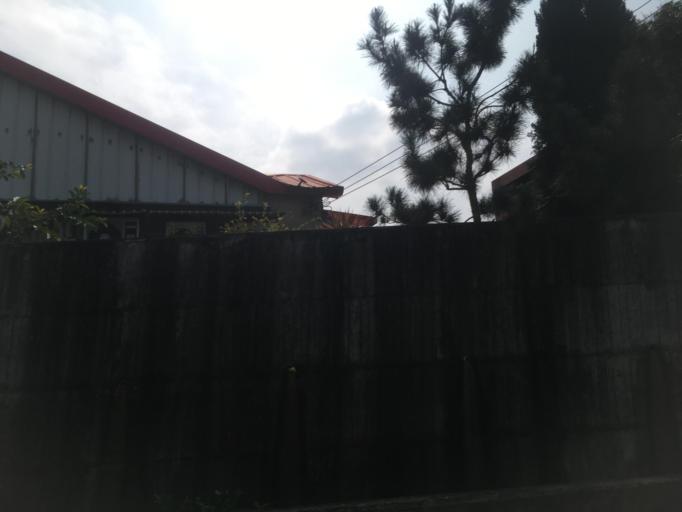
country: TW
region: Taiwan
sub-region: Yunlin
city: Douliu
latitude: 23.6983
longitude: 120.4393
